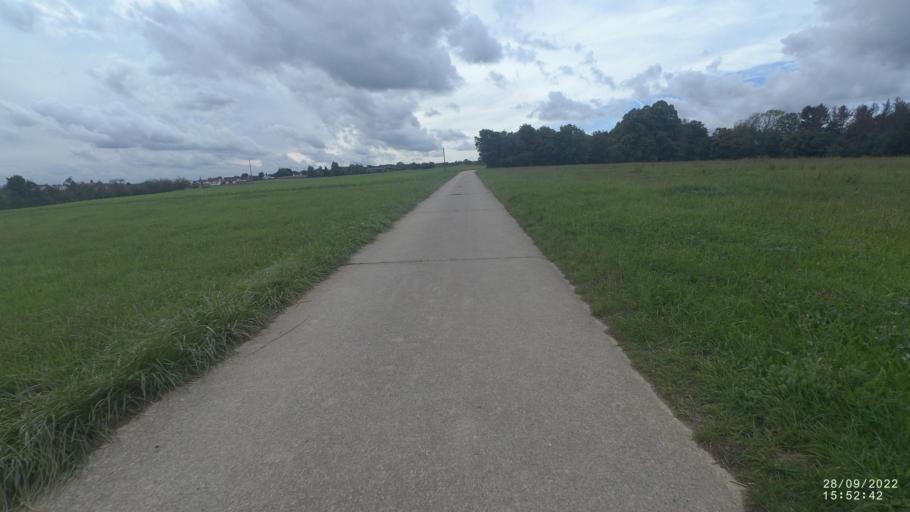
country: DE
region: Baden-Wuerttemberg
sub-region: Regierungsbezirk Stuttgart
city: Wangen
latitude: 48.7354
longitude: 9.6268
